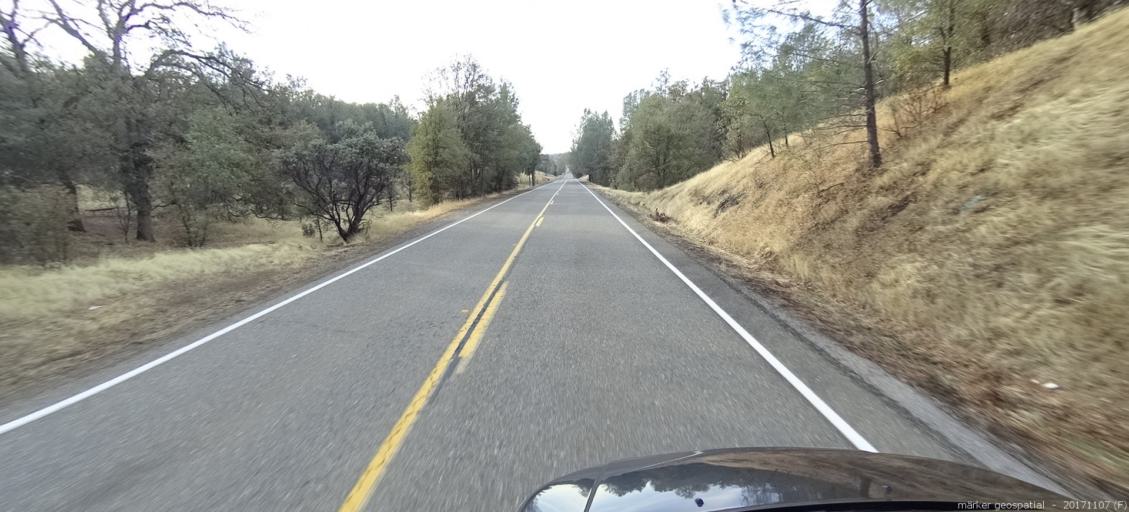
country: US
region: California
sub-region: Shasta County
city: Shasta
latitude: 40.5565
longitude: -122.4733
